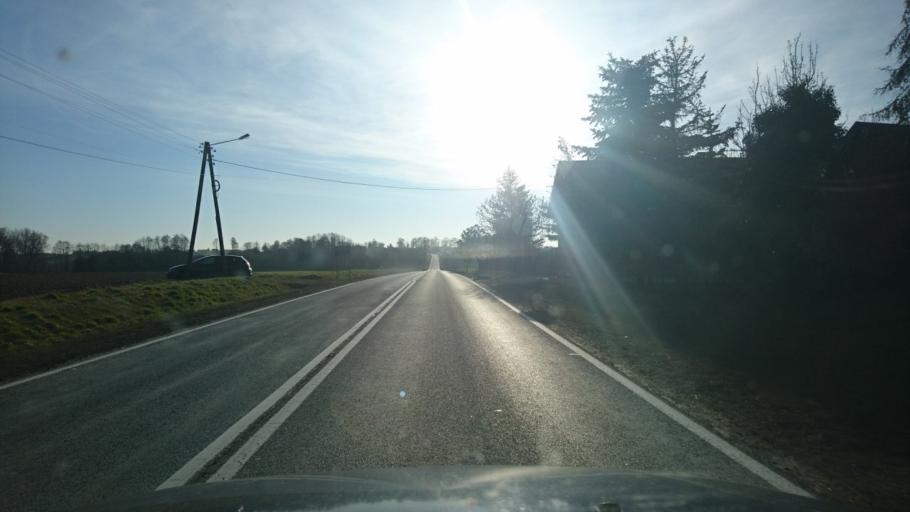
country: PL
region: Opole Voivodeship
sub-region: Powiat oleski
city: Dalachow
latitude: 51.0495
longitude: 18.5977
